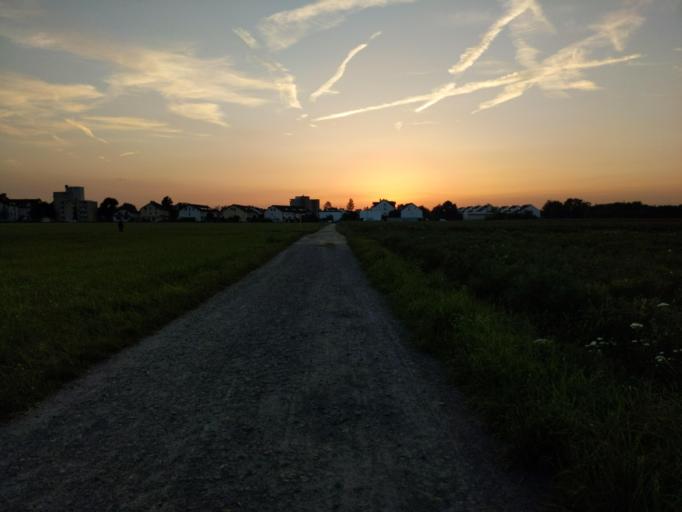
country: DE
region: Hesse
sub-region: Regierungsbezirk Darmstadt
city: Rodgau
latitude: 50.0513
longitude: 8.9023
